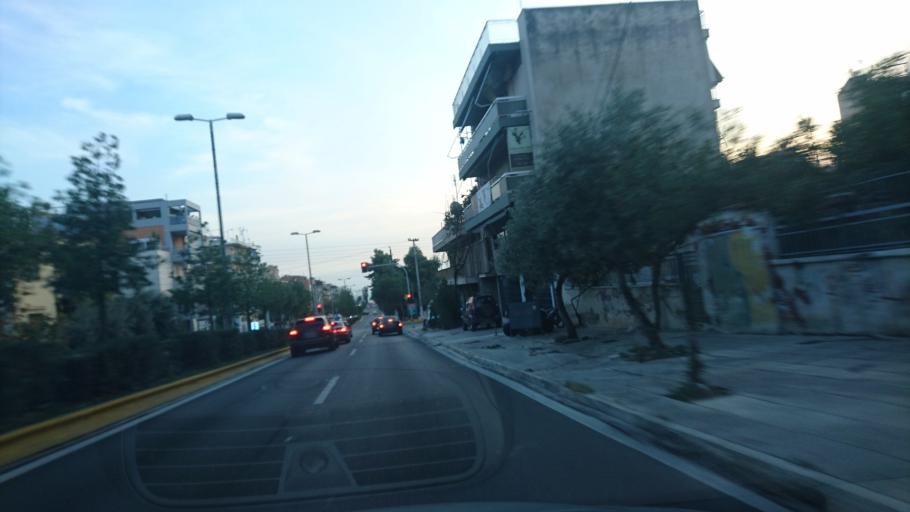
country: GR
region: Attica
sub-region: Nomarchia Athinas
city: Ilioupoli
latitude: 37.9412
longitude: 23.7616
